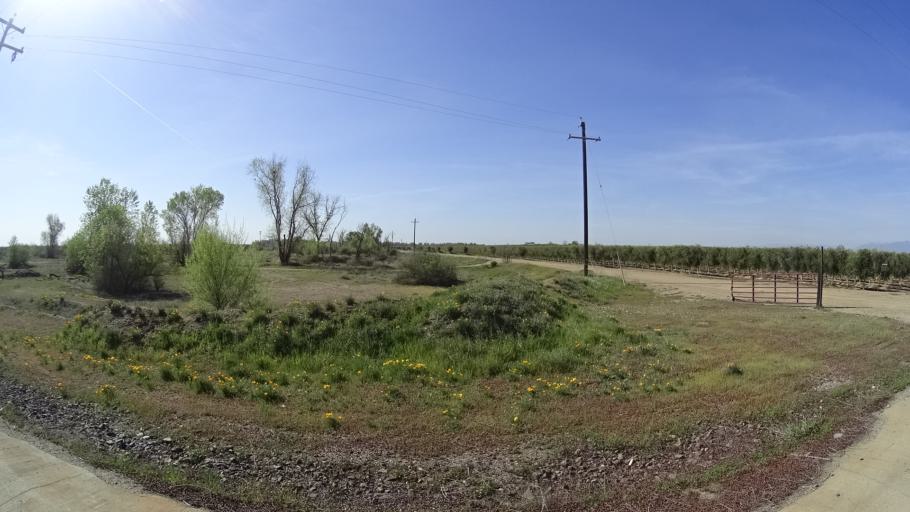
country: US
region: California
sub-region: Glenn County
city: Willows
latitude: 39.6114
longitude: -122.2023
